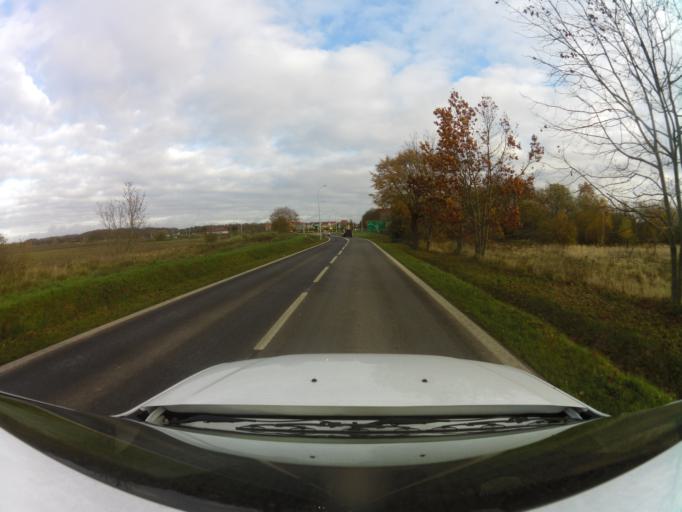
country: PL
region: West Pomeranian Voivodeship
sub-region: Powiat gryficki
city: Trzebiatow
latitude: 54.0486
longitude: 15.2539
